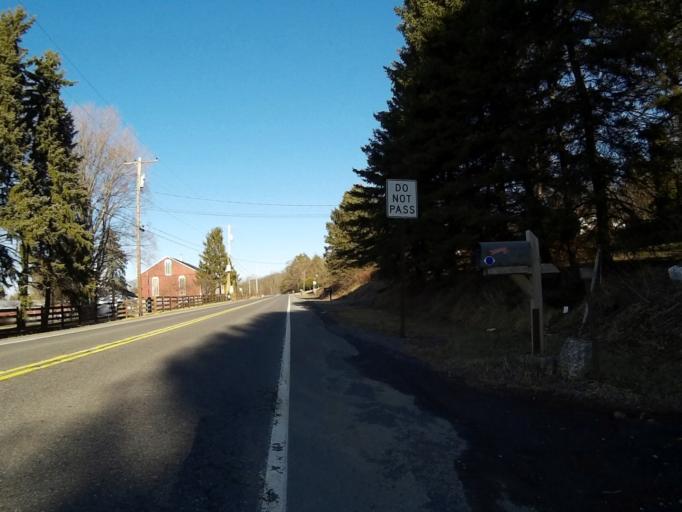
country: US
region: Pennsylvania
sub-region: Centre County
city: Pine Grove Mills
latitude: 40.7254
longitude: -77.9064
